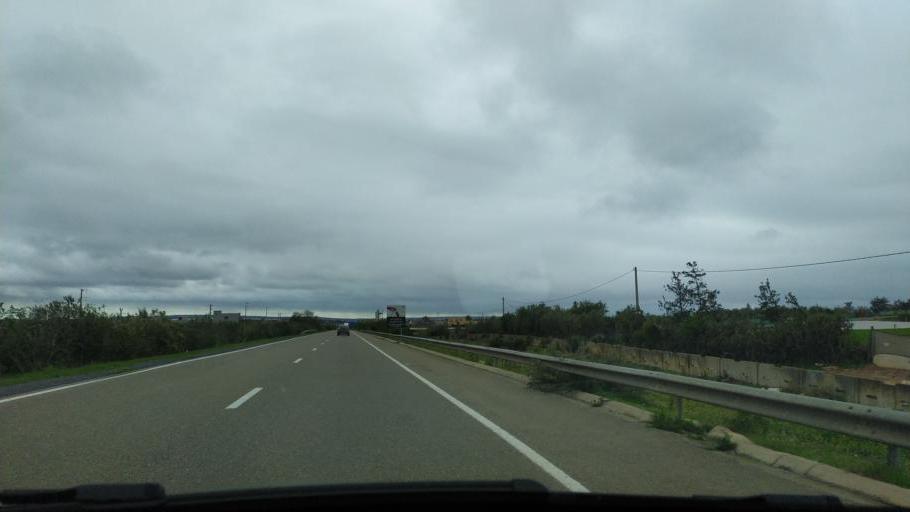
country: MA
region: Gharb-Chrarda-Beni Hssen
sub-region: Kenitra Province
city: Lalla Mimouna
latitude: 34.8699
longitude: -6.2174
